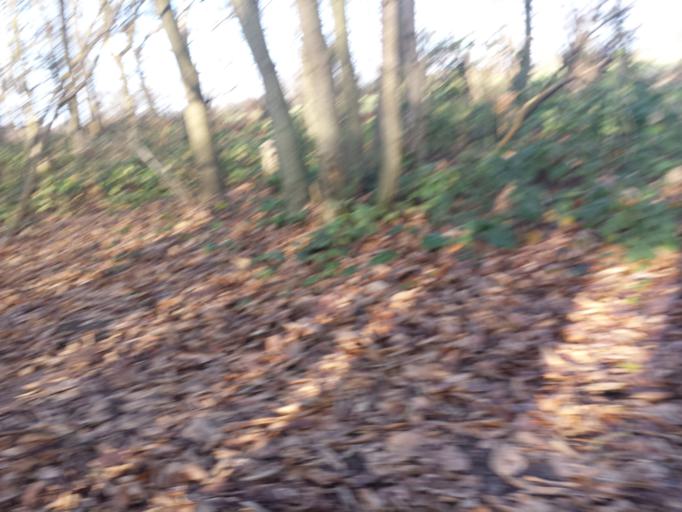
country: GB
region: England
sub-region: Essex
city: Alresford
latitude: 51.8590
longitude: 0.9878
